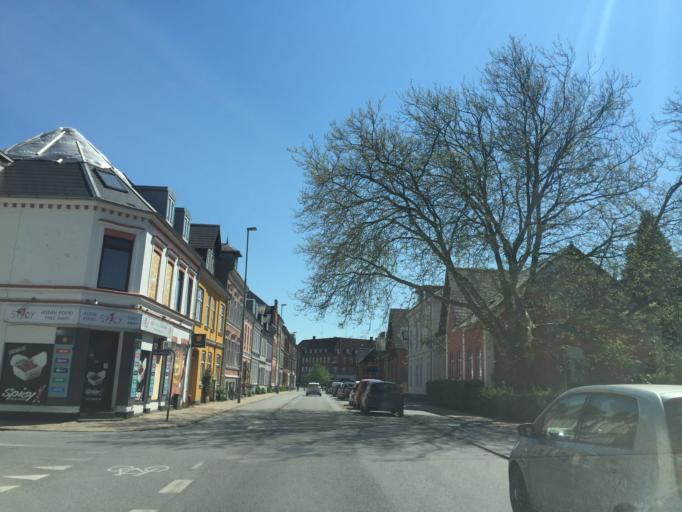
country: DK
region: South Denmark
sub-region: Odense Kommune
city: Odense
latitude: 55.3921
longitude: 10.3910
